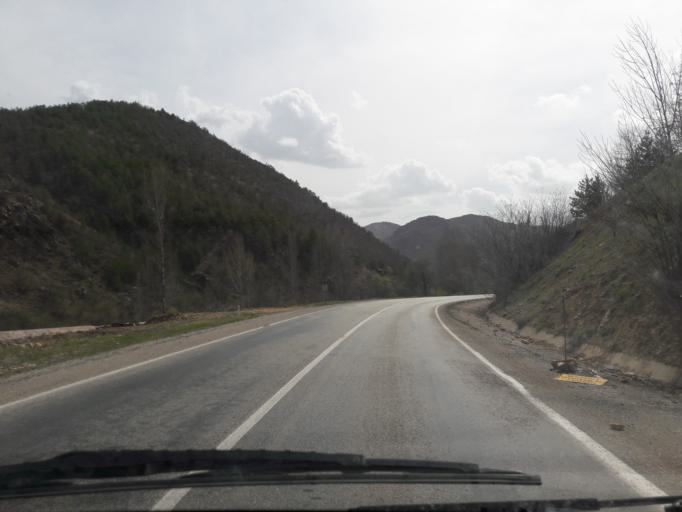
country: TR
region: Gumushane
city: Kale
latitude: 40.3935
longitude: 39.5876
